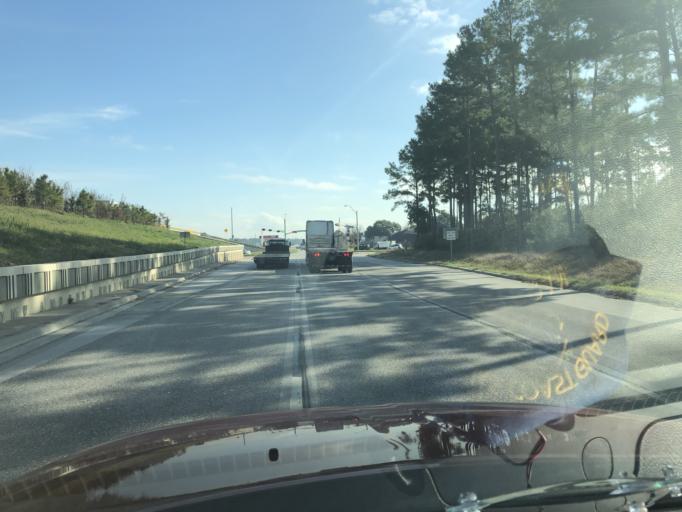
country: US
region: Texas
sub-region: Harris County
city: Tomball
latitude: 30.0514
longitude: -95.6108
